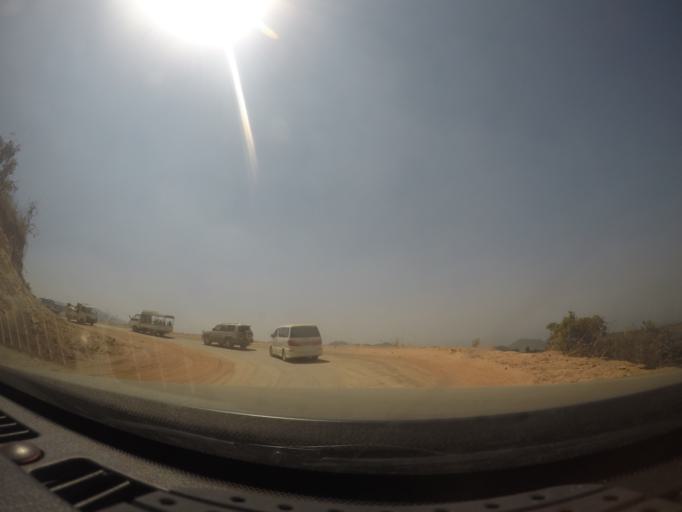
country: MM
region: Shan
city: Taunggyi
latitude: 20.8086
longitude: 97.2773
